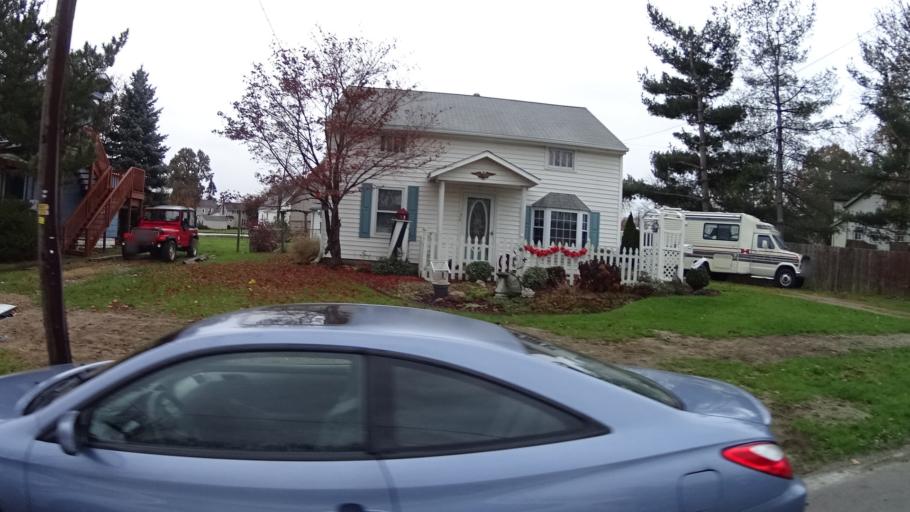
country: US
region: Ohio
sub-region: Lorain County
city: Elyria
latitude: 41.3828
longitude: -82.1253
